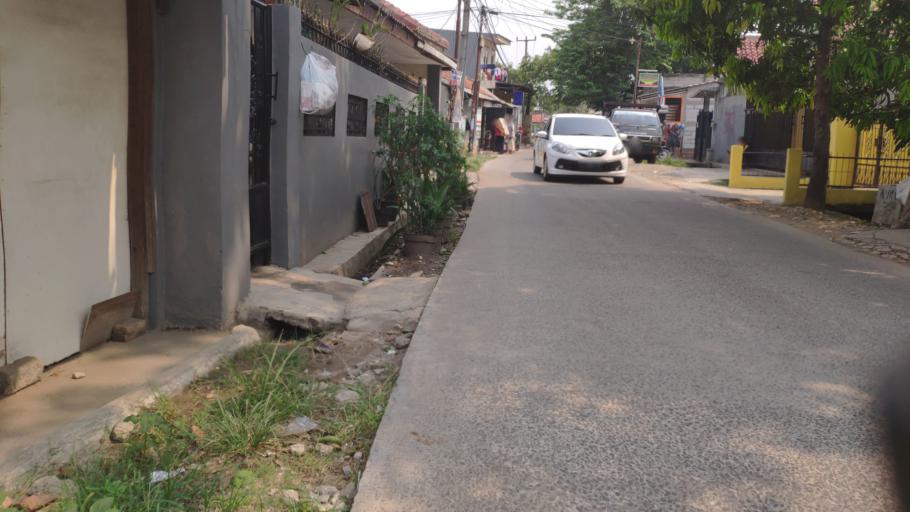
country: ID
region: West Java
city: Depok
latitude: -6.3853
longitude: 106.8047
